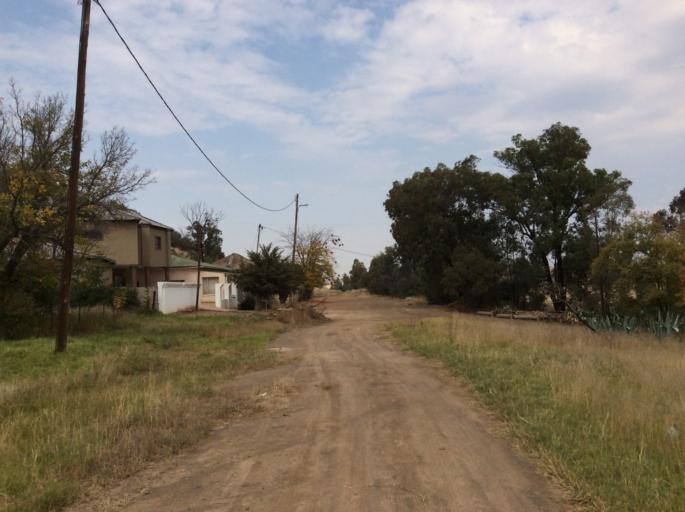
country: LS
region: Mafeteng
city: Mafeteng
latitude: -29.7313
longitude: 27.0432
